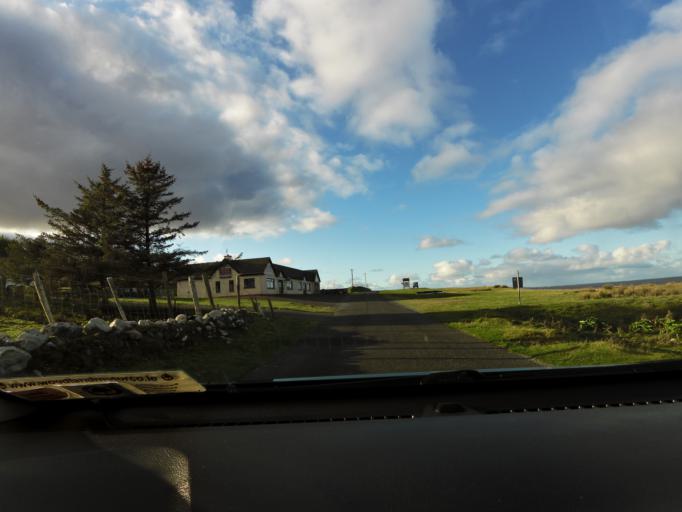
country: IE
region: Connaught
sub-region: Maigh Eo
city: Belmullet
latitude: 54.0114
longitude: -9.9934
